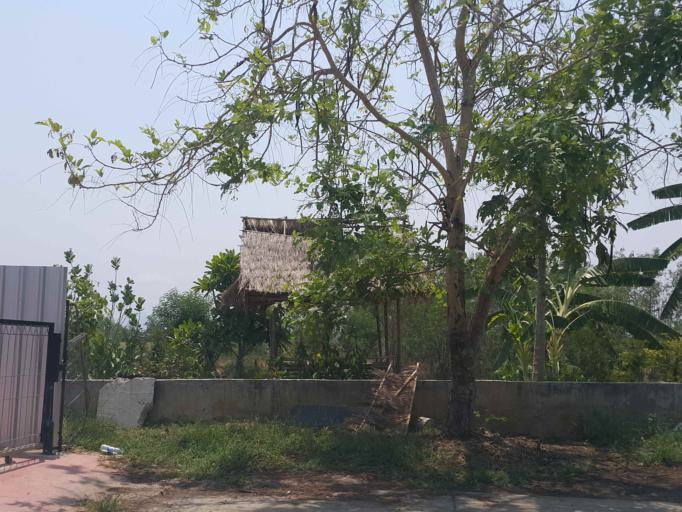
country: TH
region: Chiang Mai
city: San Kamphaeng
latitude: 18.7446
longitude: 99.0874
